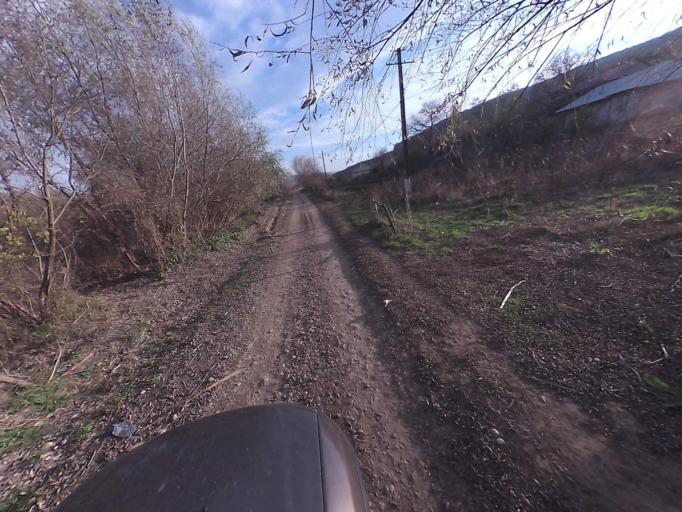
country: RO
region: Vaslui
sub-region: Comuna Gherghesti
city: Gherghesti
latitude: 46.4897
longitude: 27.5288
